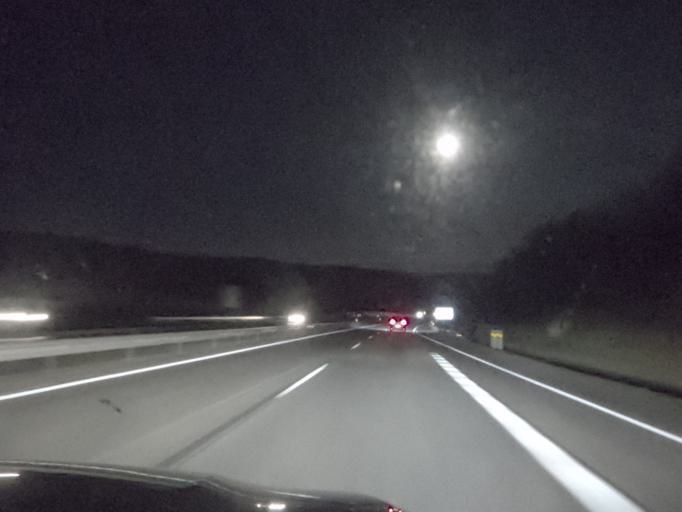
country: ES
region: Galicia
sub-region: Provincia de Ourense
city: Allariz
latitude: 42.2080
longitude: -7.8165
